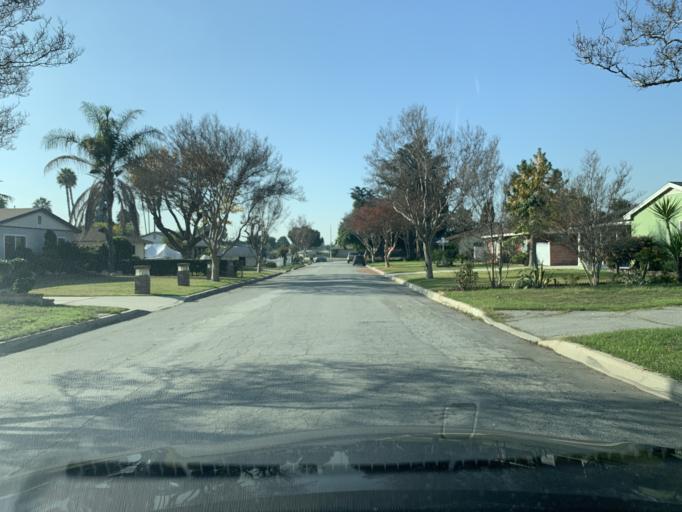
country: US
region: California
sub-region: Los Angeles County
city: Covina
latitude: 34.0740
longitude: -117.8974
